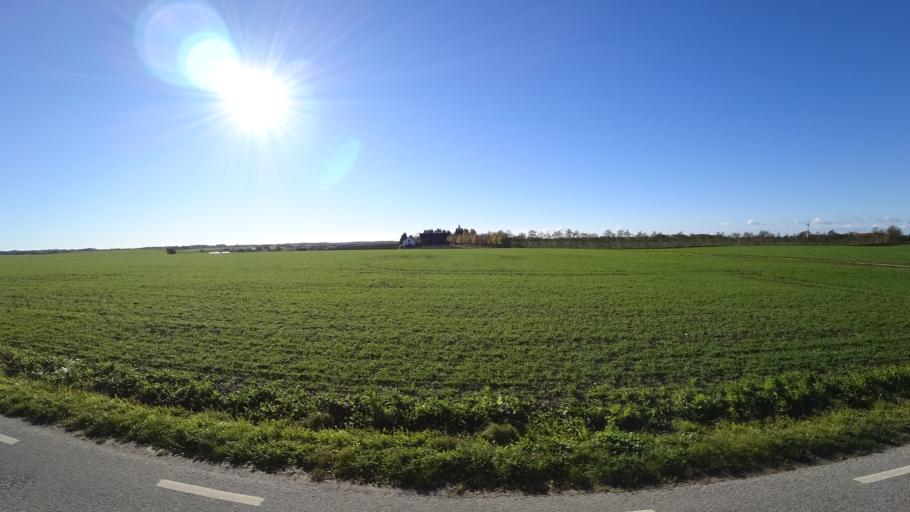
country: SE
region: Skane
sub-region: Svedala Kommun
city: Klagerup
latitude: 55.6162
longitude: 13.2997
